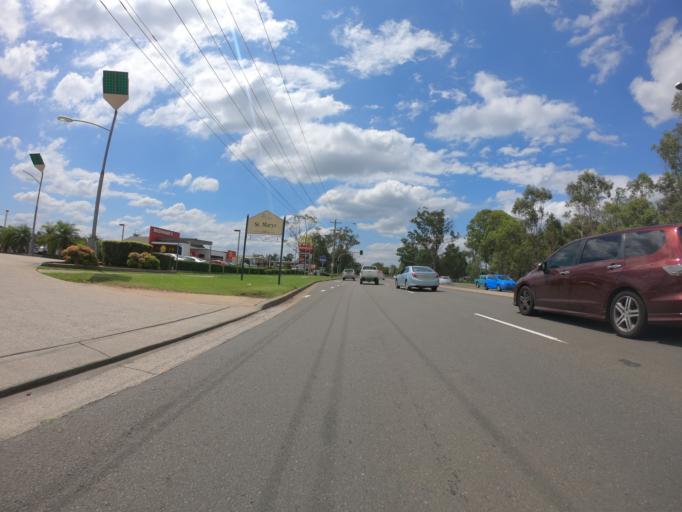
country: AU
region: New South Wales
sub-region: Penrith Municipality
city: Werrington County
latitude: -33.7813
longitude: 150.7715
